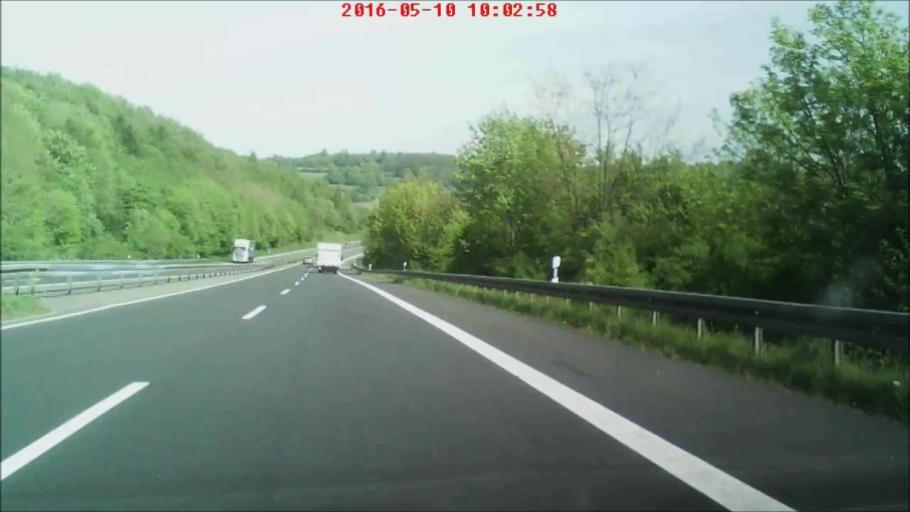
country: DE
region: Hesse
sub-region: Regierungsbezirk Darmstadt
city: Schluchtern
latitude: 50.3543
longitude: 9.5022
